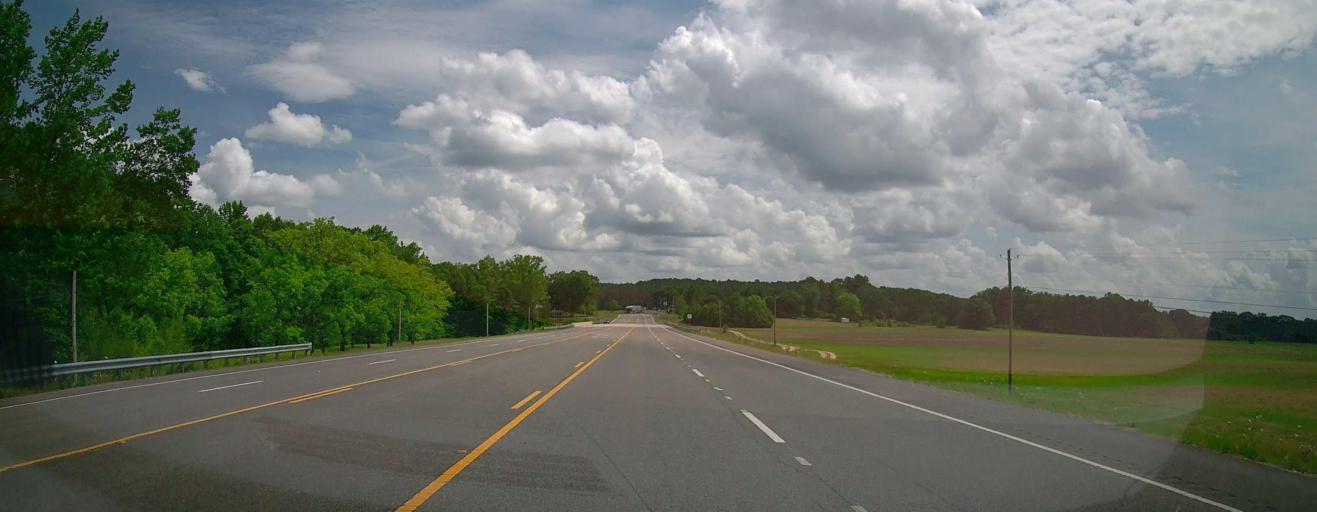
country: US
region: Alabama
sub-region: Marion County
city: Hamilton
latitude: 34.1053
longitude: -87.9891
